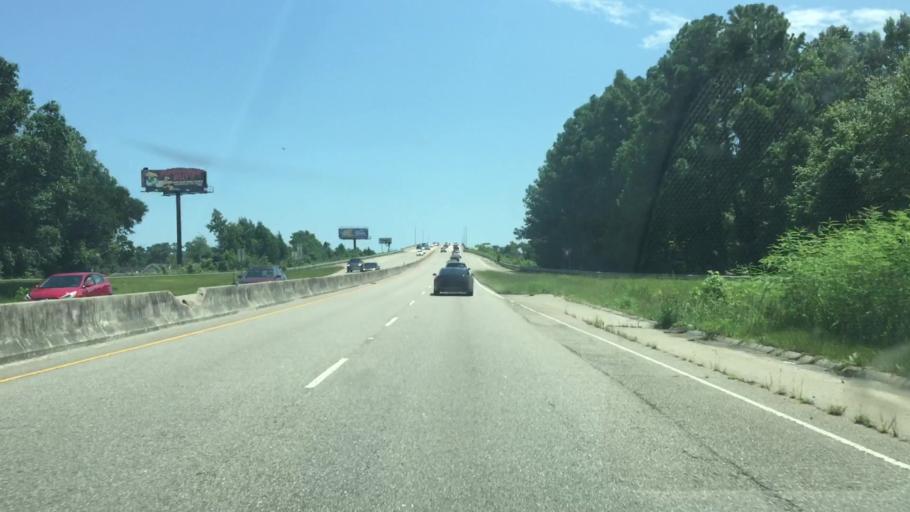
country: US
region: South Carolina
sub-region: Horry County
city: Little River
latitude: 33.8579
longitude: -78.6563
